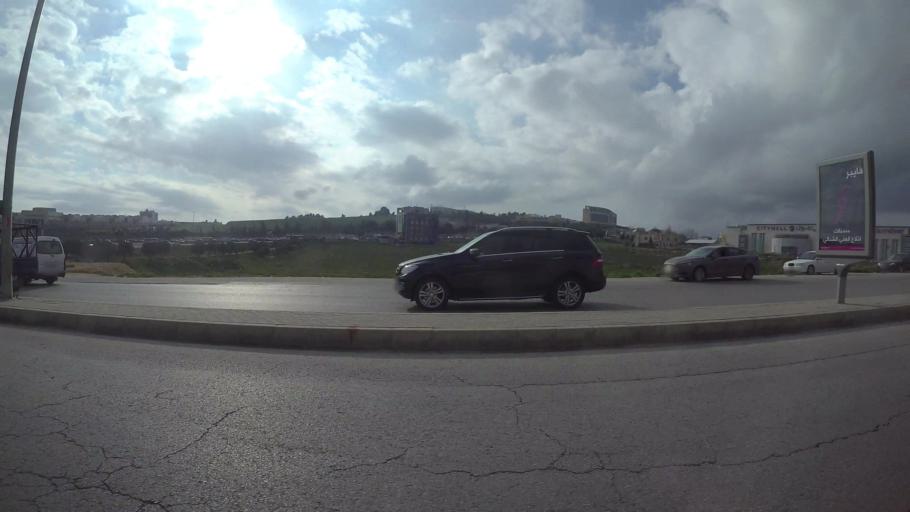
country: JO
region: Amman
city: Wadi as Sir
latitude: 31.9772
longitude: 35.8405
